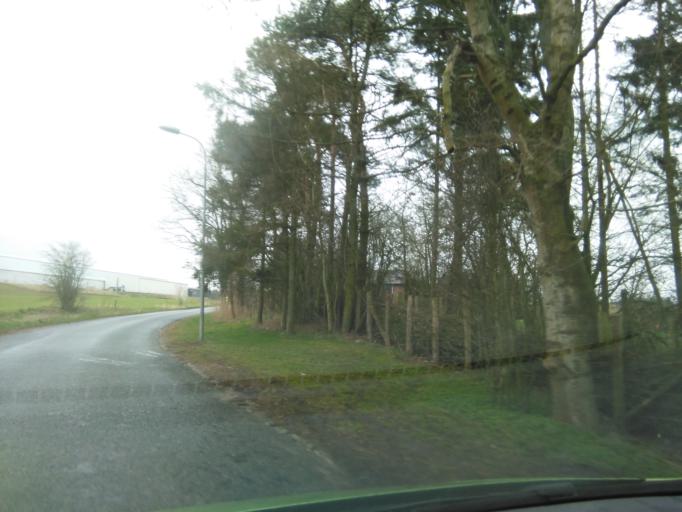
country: DK
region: Central Jutland
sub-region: Arhus Kommune
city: Kolt
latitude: 56.1443
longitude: 10.0526
